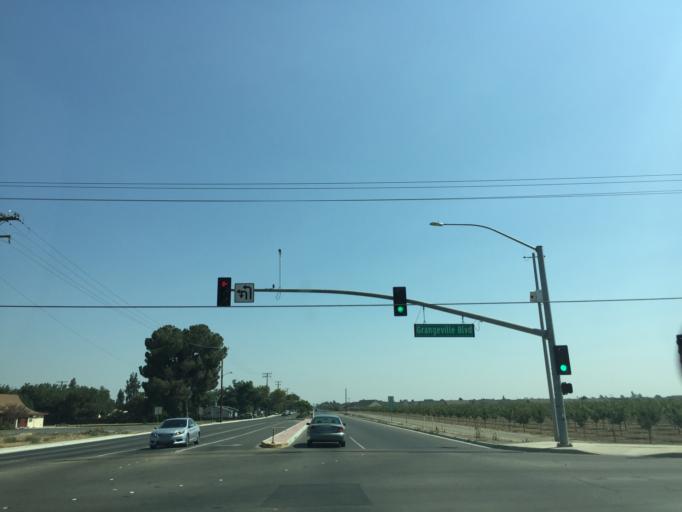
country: US
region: California
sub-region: Kings County
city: Hanford
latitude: 36.3428
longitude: -119.6729
